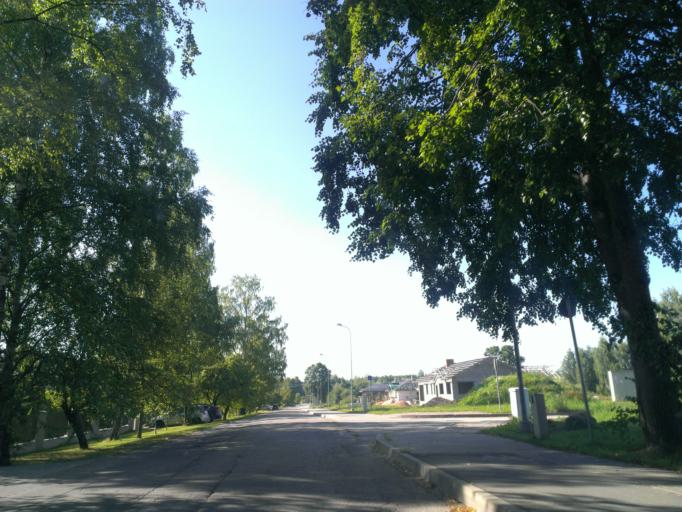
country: LV
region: Sigulda
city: Sigulda
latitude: 57.1650
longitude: 24.8760
